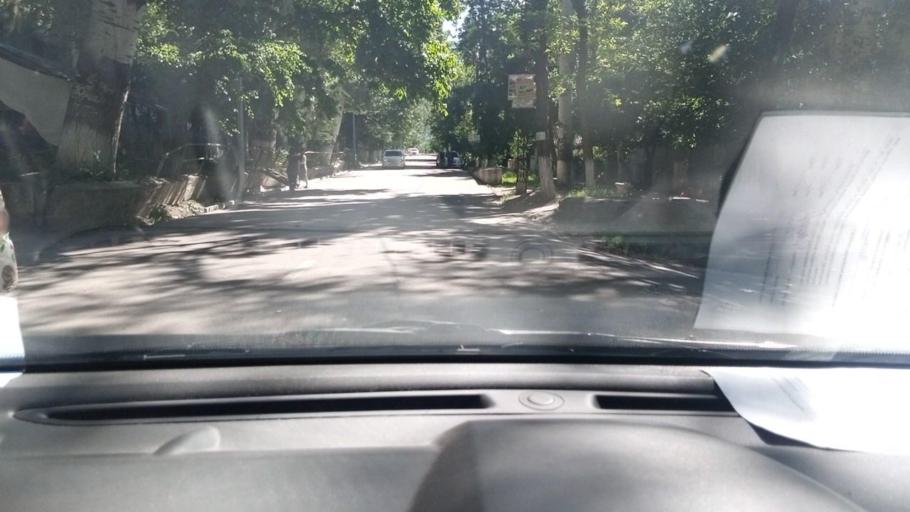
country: UZ
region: Toshkent
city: Yangiobod
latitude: 41.1199
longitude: 70.0954
